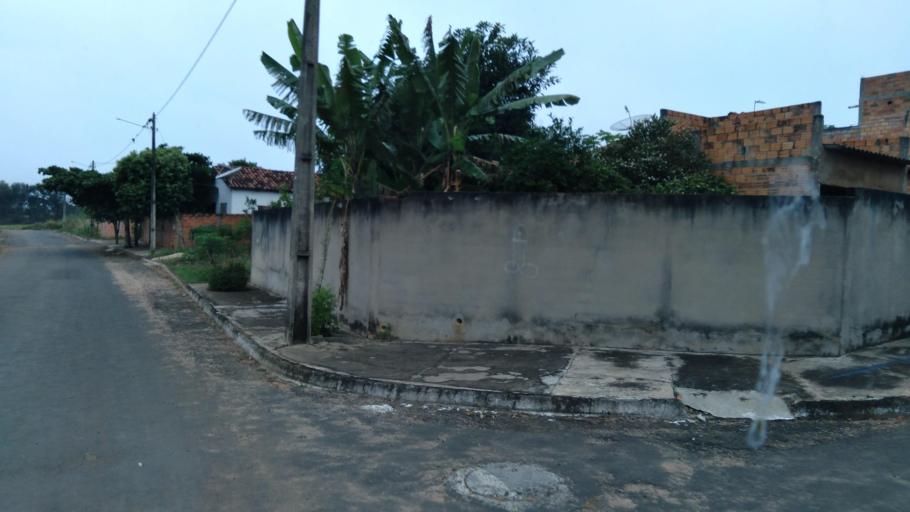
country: BR
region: Goias
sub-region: Mineiros
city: Mineiros
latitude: -17.5720
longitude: -52.5446
